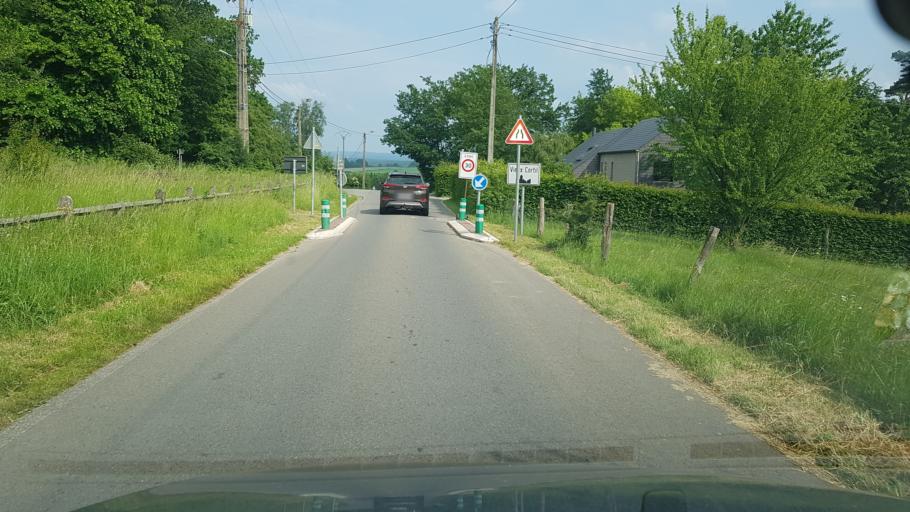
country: BE
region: Wallonia
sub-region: Province de Liege
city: Theux
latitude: 50.5142
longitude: 5.7781
